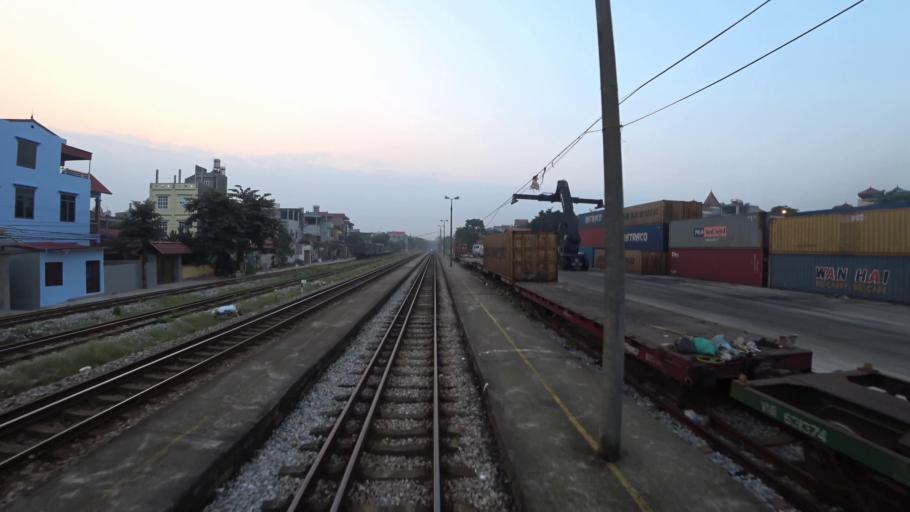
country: VN
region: Ha Noi
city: Dong Anh
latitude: 21.1536
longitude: 105.8515
